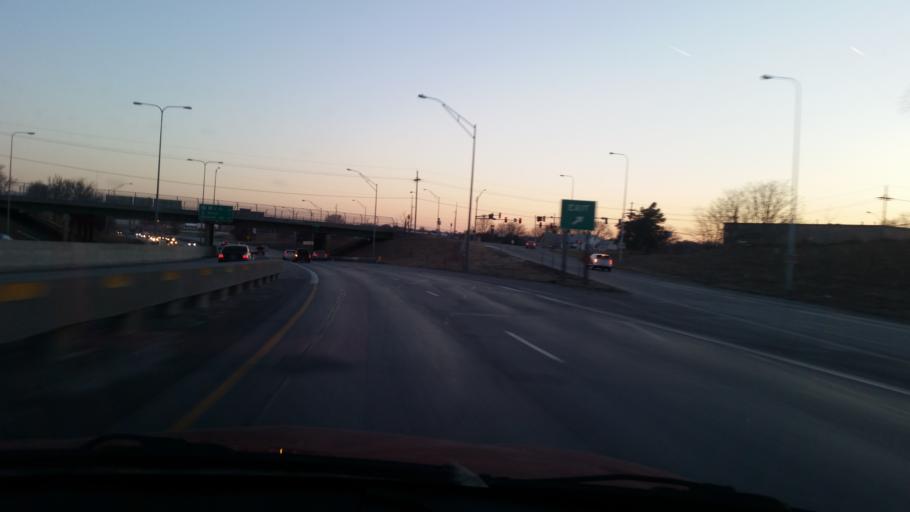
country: US
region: Nebraska
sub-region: Douglas County
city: Omaha
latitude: 41.2211
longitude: -95.9532
